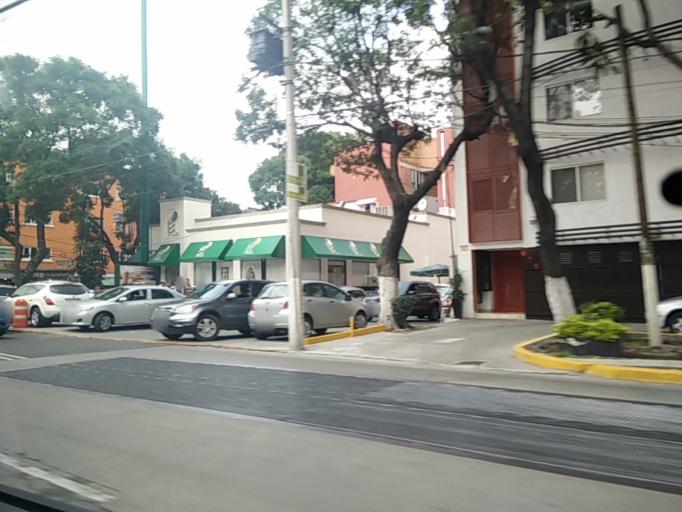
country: MX
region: Mexico City
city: Benito Juarez
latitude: 19.3944
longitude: -99.1562
